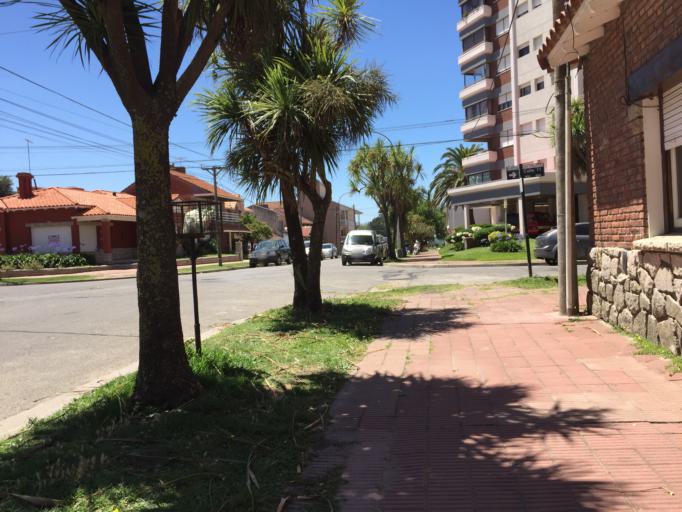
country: AR
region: Buenos Aires
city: Miramar
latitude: -38.2692
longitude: -57.8314
